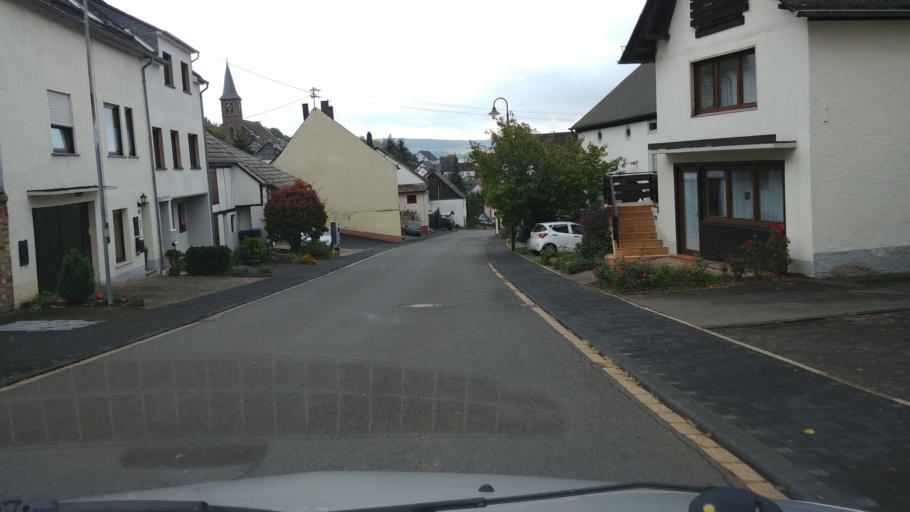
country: DE
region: Rheinland-Pfalz
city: Horath
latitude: 49.8130
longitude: 6.9867
